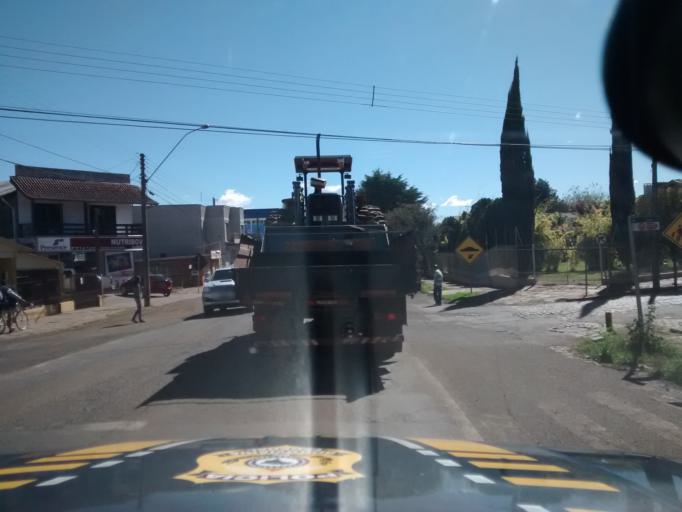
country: BR
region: Rio Grande do Sul
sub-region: Vacaria
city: Vacaria
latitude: -28.5089
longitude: -50.9390
